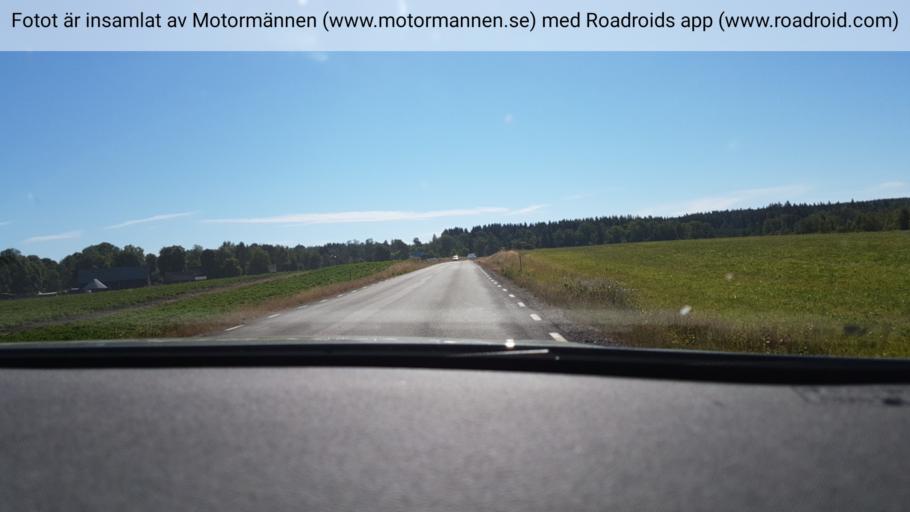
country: SE
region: Vaestra Goetaland
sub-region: Tidaholms Kommun
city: Tidaholm
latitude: 58.1398
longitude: 14.0103
